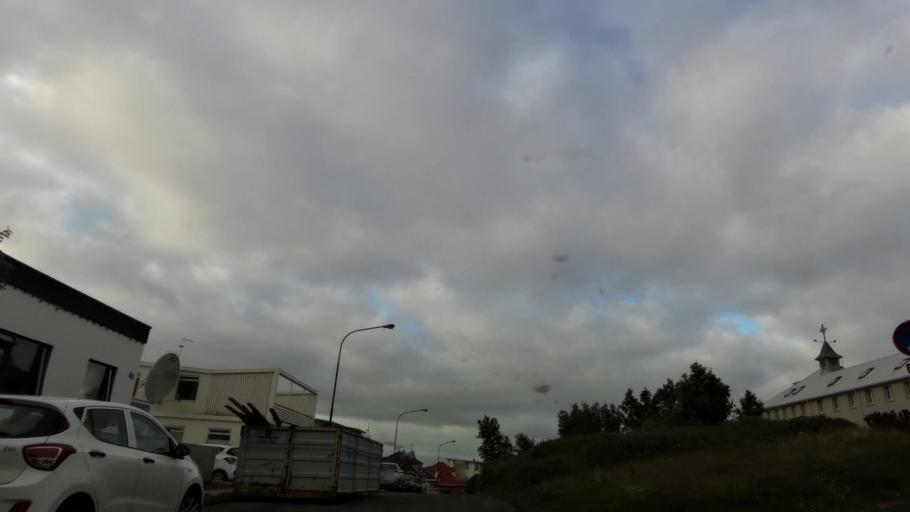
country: IS
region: Capital Region
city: Hafnarfjoerdur
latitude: 64.0620
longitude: -21.9520
